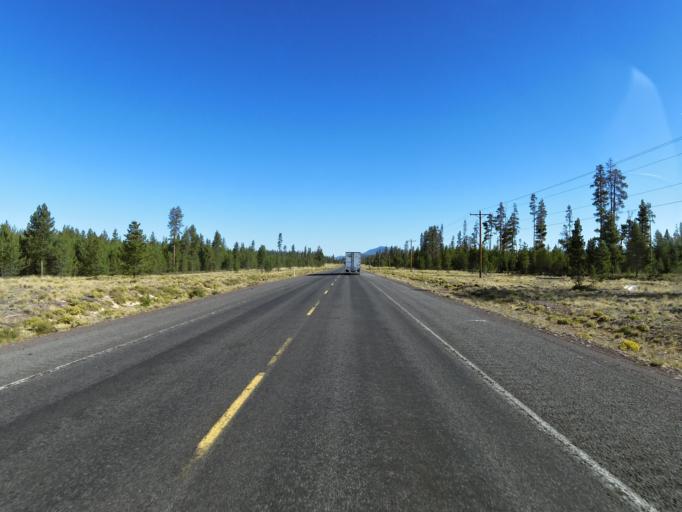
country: US
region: Oregon
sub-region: Deschutes County
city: La Pine
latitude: 43.1609
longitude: -121.7919
